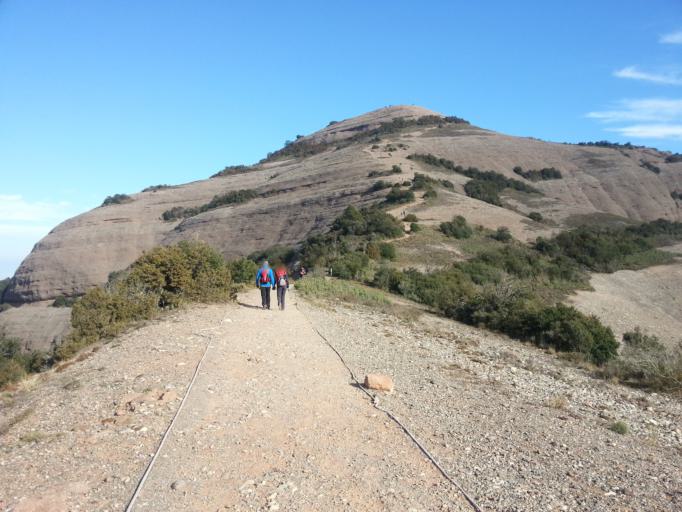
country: ES
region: Catalonia
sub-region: Provincia de Barcelona
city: Mura
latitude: 41.6726
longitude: 2.0005
